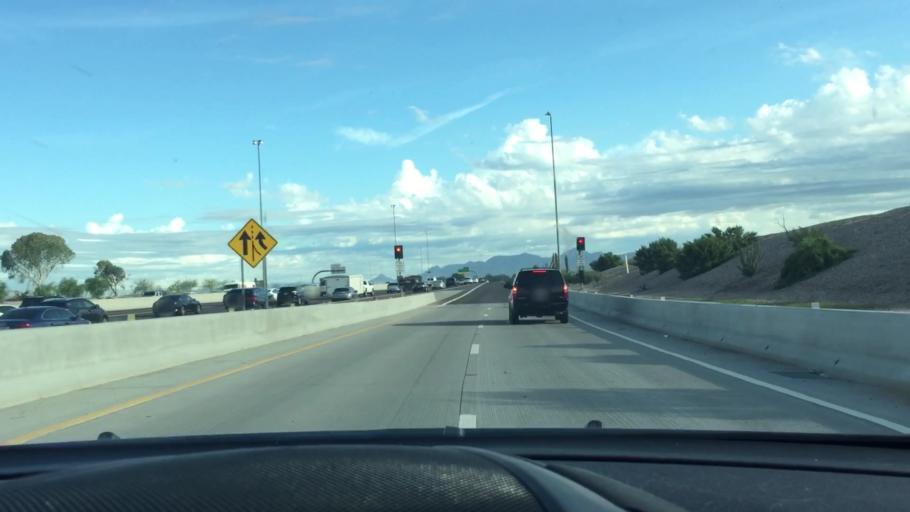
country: US
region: Arizona
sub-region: Maricopa County
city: Scottsdale
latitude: 33.4829
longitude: -111.8890
